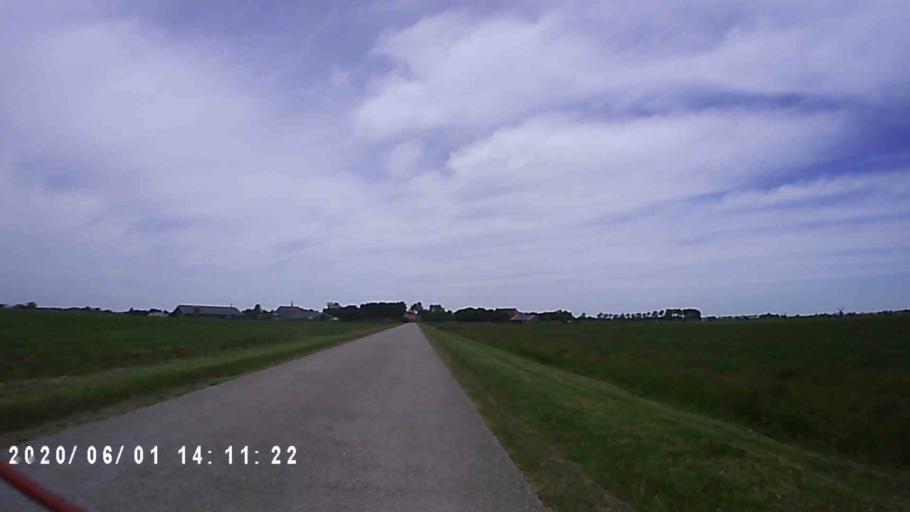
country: NL
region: Friesland
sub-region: Gemeente Littenseradiel
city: Winsum
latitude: 53.1267
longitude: 5.6493
